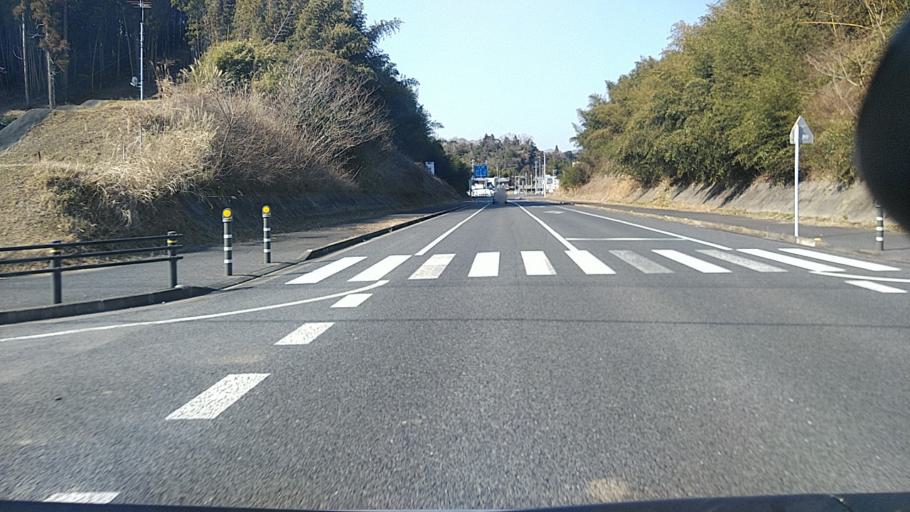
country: JP
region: Chiba
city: Mobara
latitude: 35.4035
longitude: 140.2400
